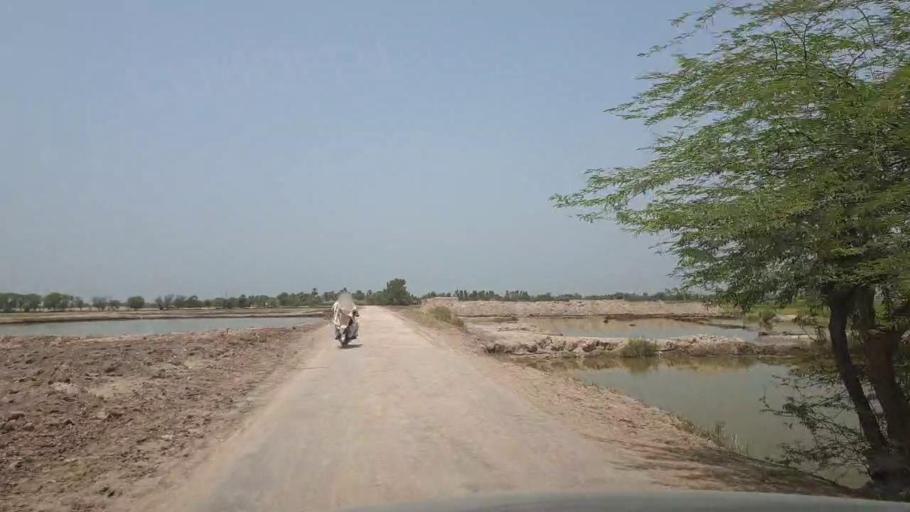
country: PK
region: Sindh
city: Garhi Yasin
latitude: 27.8658
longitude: 68.4574
